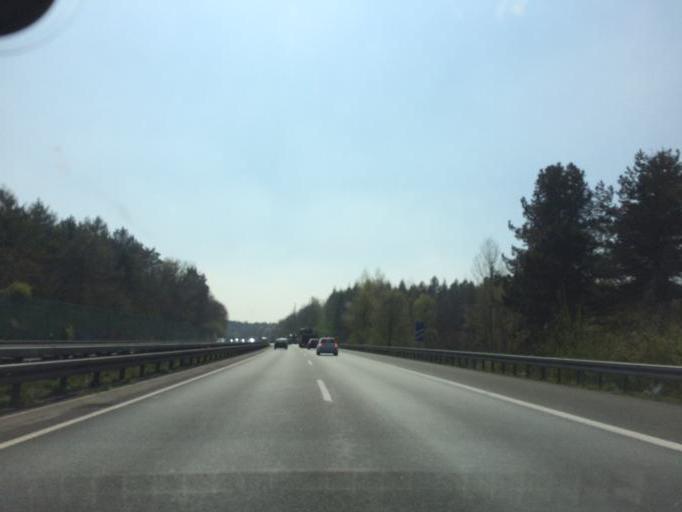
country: DE
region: North Rhine-Westphalia
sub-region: Regierungsbezirk Munster
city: Haltern
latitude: 51.7405
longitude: 7.1534
